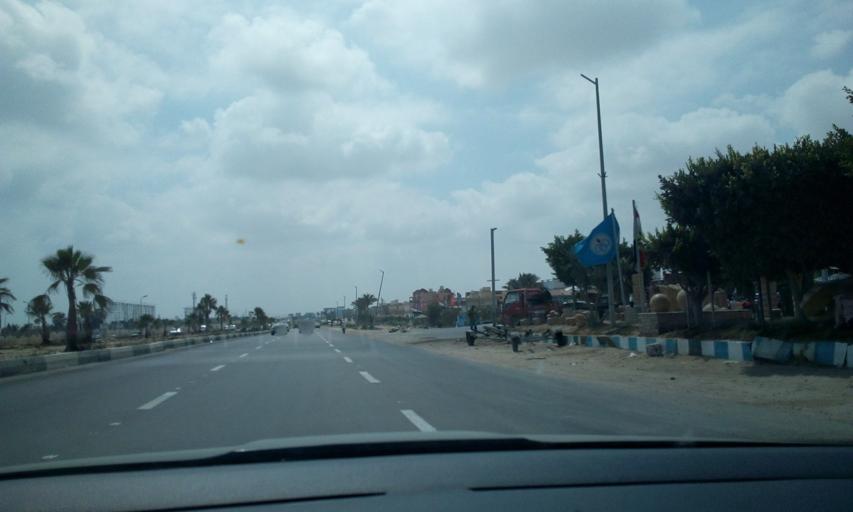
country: EG
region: Muhafazat Matruh
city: Al `Alamayn
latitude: 30.8335
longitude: 28.9631
